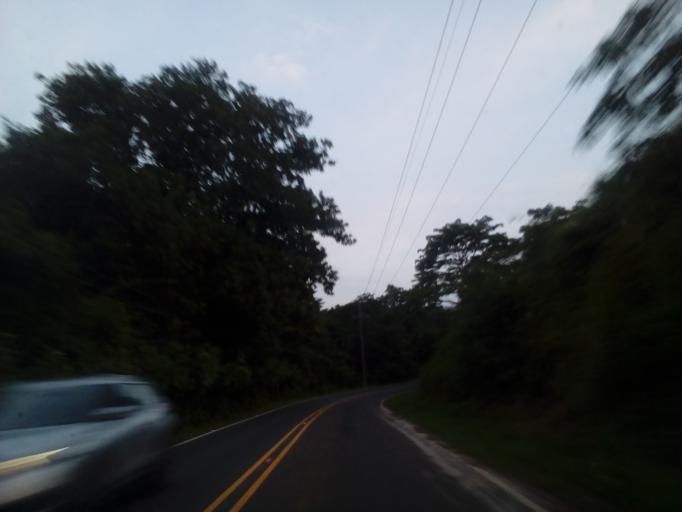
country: CR
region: Guanacaste
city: Hojancha
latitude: 10.0142
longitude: -85.5008
